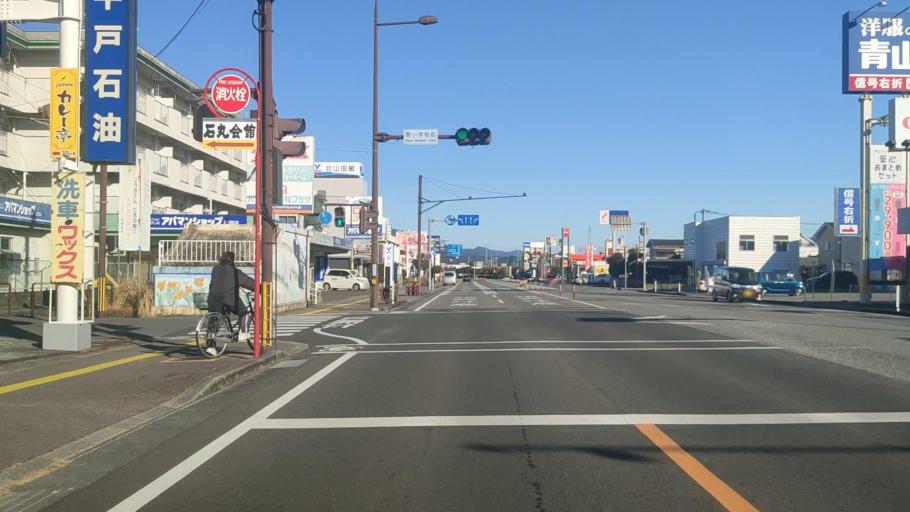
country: JP
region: Miyazaki
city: Nobeoka
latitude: 32.5738
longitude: 131.6836
